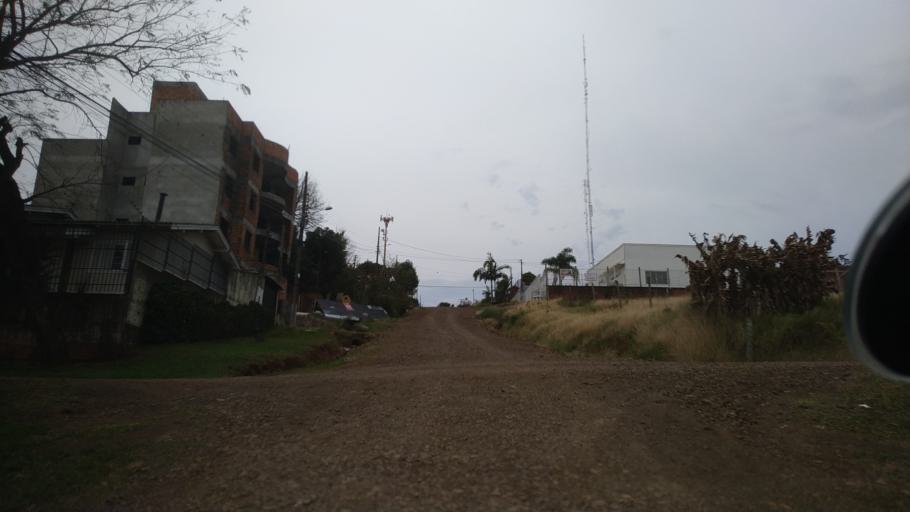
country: BR
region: Santa Catarina
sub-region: Chapeco
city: Chapeco
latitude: -27.1180
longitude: -52.5955
